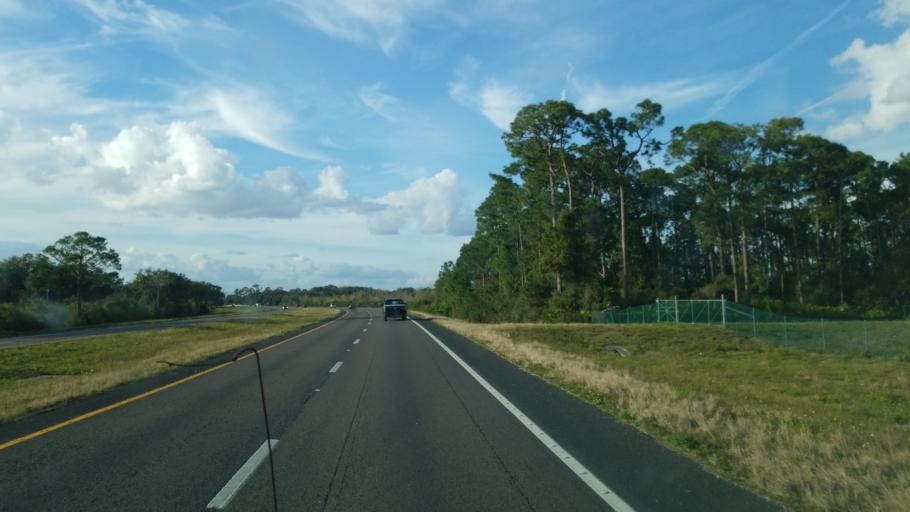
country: US
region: Florida
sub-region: Osceola County
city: Saint Cloud
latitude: 28.2294
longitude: -81.1845
